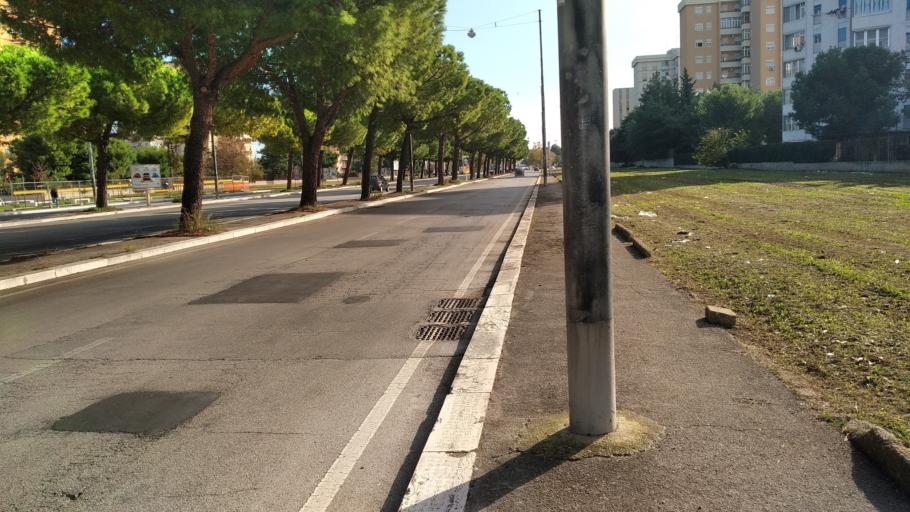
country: IT
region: Apulia
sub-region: Provincia di Bari
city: Triggiano
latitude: 41.1042
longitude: 16.9041
